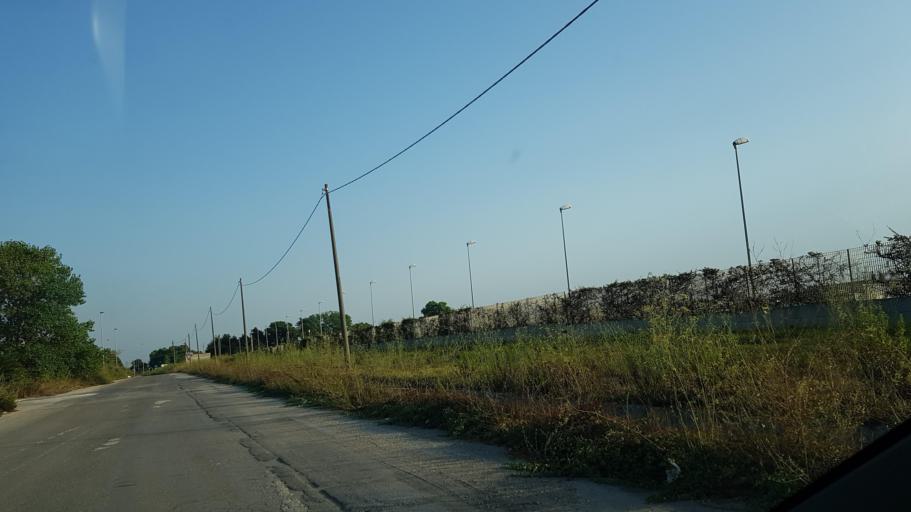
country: IT
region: Apulia
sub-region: Provincia di Brindisi
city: Materdomini
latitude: 40.6378
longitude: 17.9714
